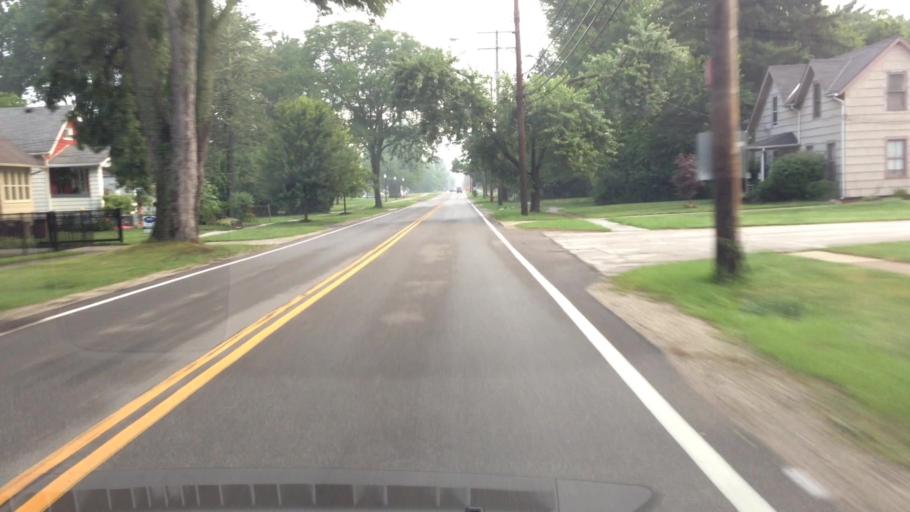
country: US
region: Ohio
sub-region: Cuyahoga County
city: Berea
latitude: 41.3665
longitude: -81.8440
